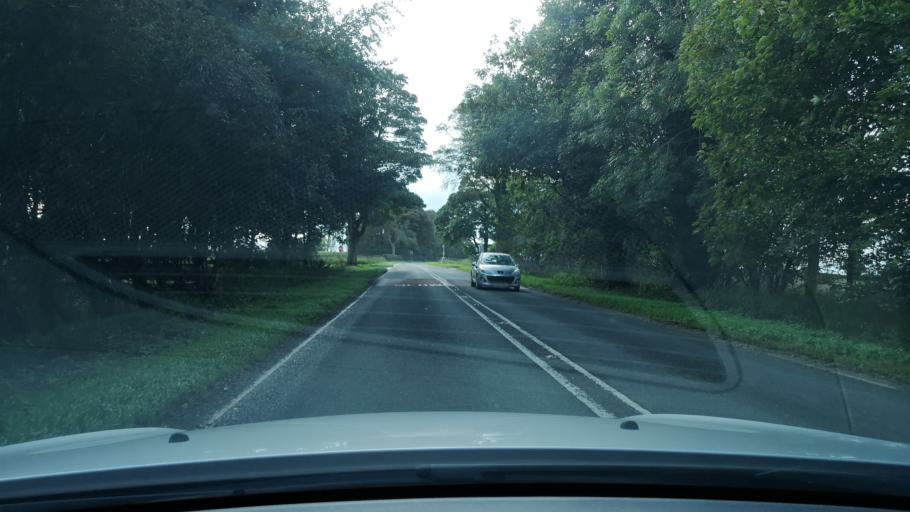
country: GB
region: England
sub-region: East Riding of Yorkshire
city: South Cave
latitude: 53.8041
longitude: -0.5608
